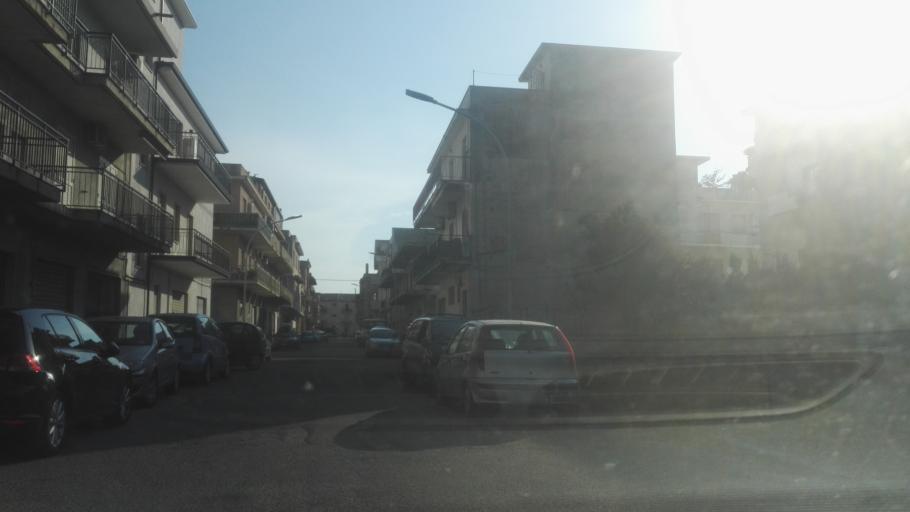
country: IT
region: Calabria
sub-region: Provincia di Reggio Calabria
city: Marina di Gioiosa Ionica
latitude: 38.3033
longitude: 16.3298
